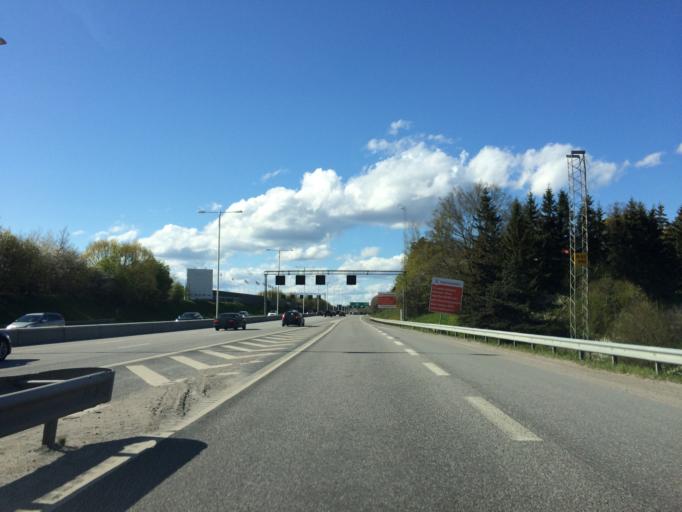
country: SE
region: Stockholm
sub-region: Solna Kommun
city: Solna
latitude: 59.3806
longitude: 18.0107
